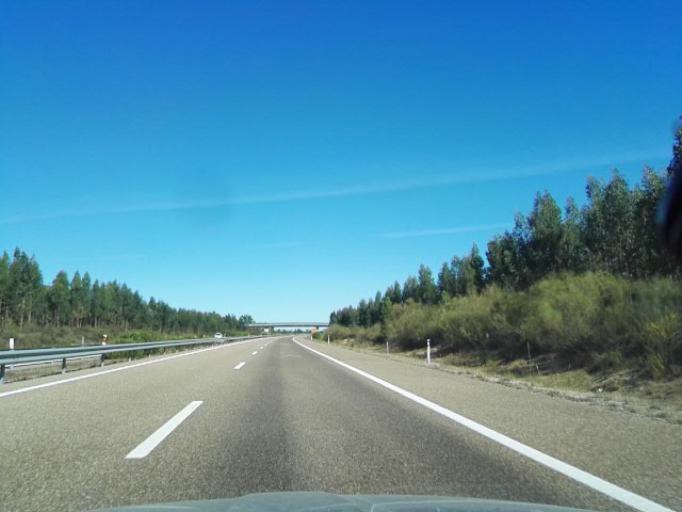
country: PT
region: Evora
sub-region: Vendas Novas
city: Vendas Novas
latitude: 38.6354
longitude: -8.6629
